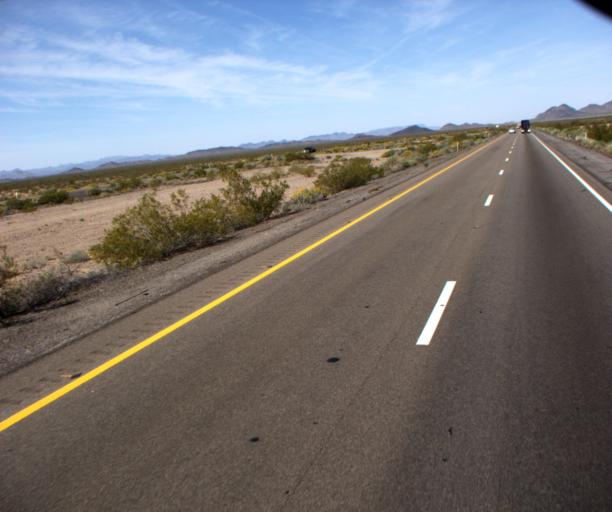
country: US
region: Arizona
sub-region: La Paz County
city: Salome
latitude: 33.5971
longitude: -113.5375
